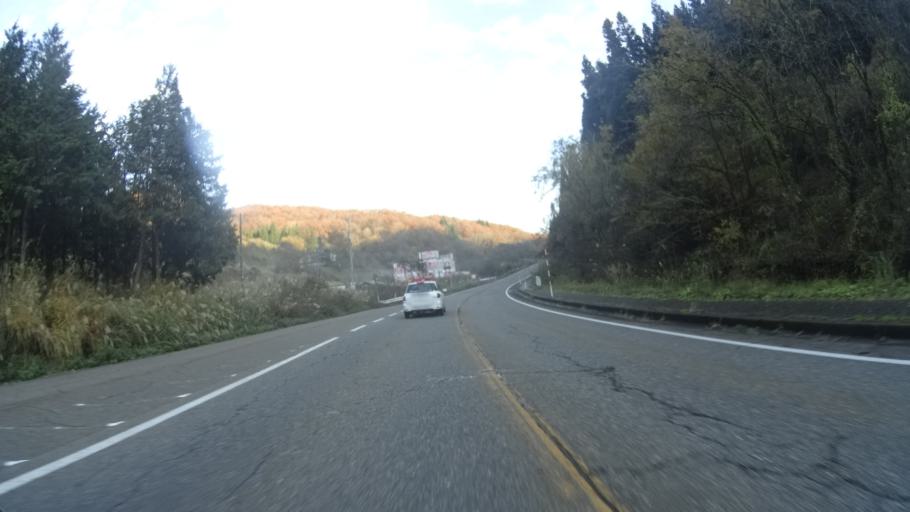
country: JP
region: Niigata
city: Kashiwazaki
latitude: 37.4131
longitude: 138.6818
